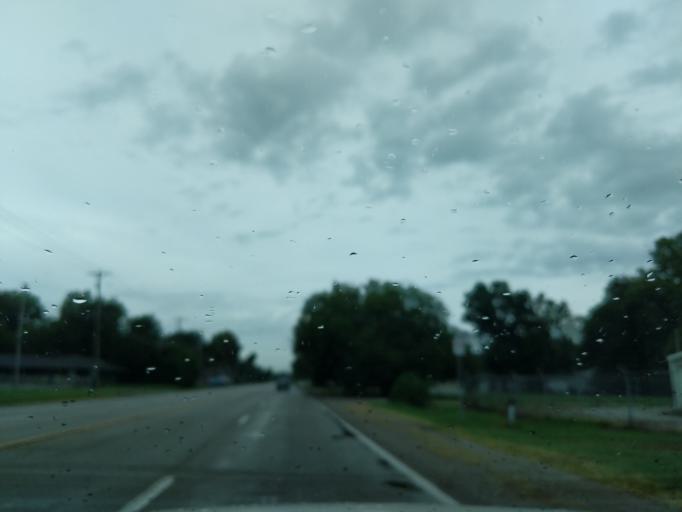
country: US
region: Illinois
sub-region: Saint Clair County
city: Fairmont City
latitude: 38.6594
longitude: -90.0833
